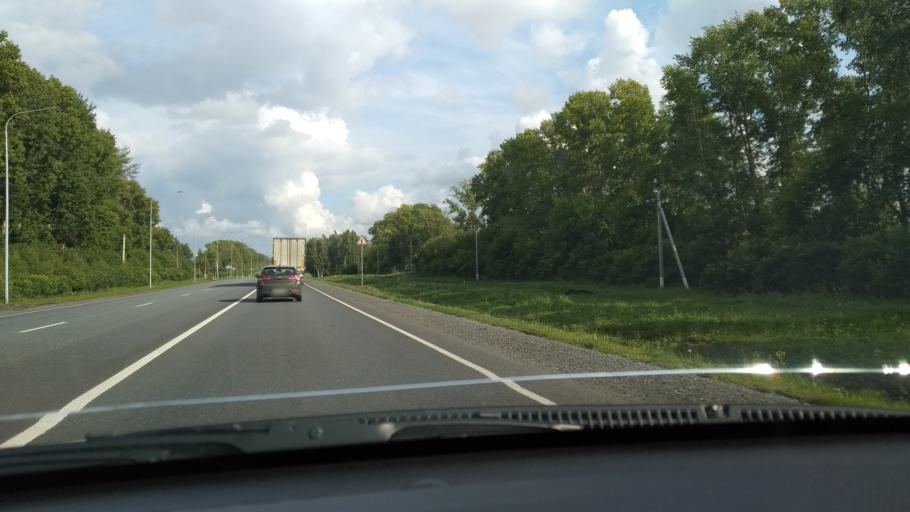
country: RU
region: Tatarstan
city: Stolbishchi
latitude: 55.6537
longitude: 49.3174
